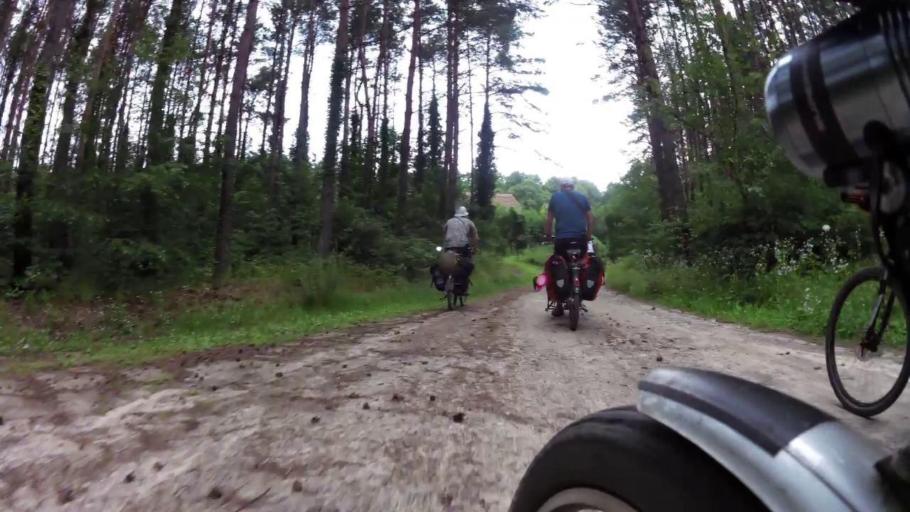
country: PL
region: West Pomeranian Voivodeship
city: Trzcinsko Zdroj
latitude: 52.8657
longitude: 14.6057
